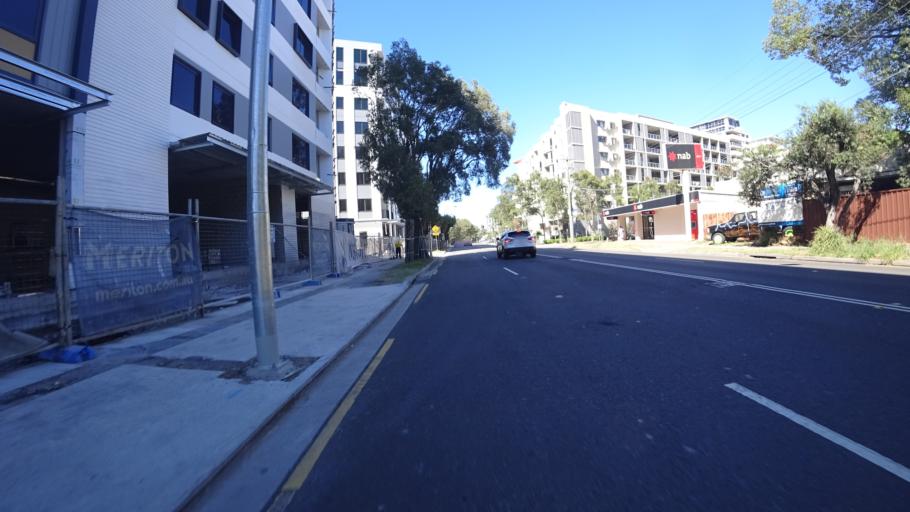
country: AU
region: New South Wales
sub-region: Botany Bay
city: Mascot
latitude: -33.9239
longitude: 151.1909
